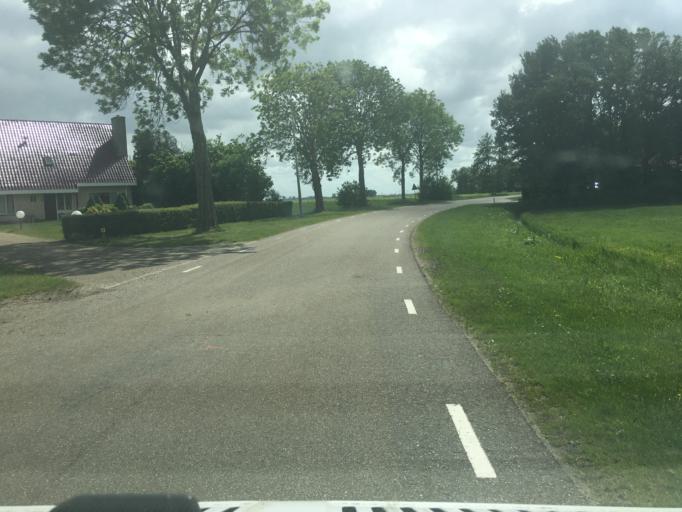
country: NL
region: Friesland
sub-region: Gemeente Heerenveen
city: Oudeschoot
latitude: 52.9093
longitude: 5.9194
